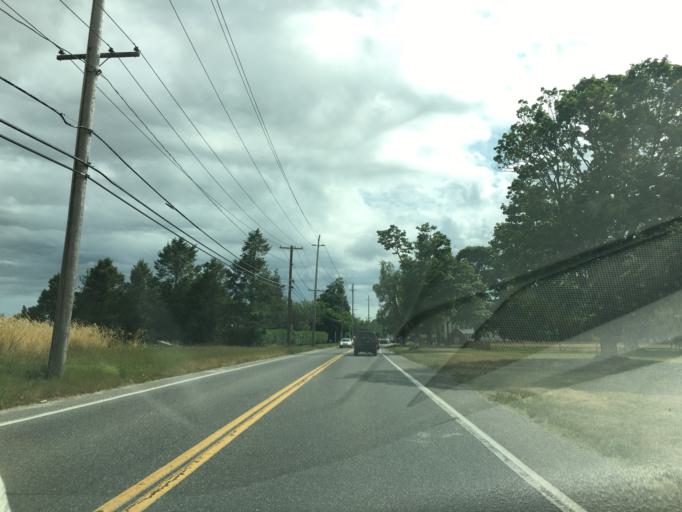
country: US
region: New York
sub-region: Suffolk County
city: Northville
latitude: 40.9740
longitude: -72.6128
